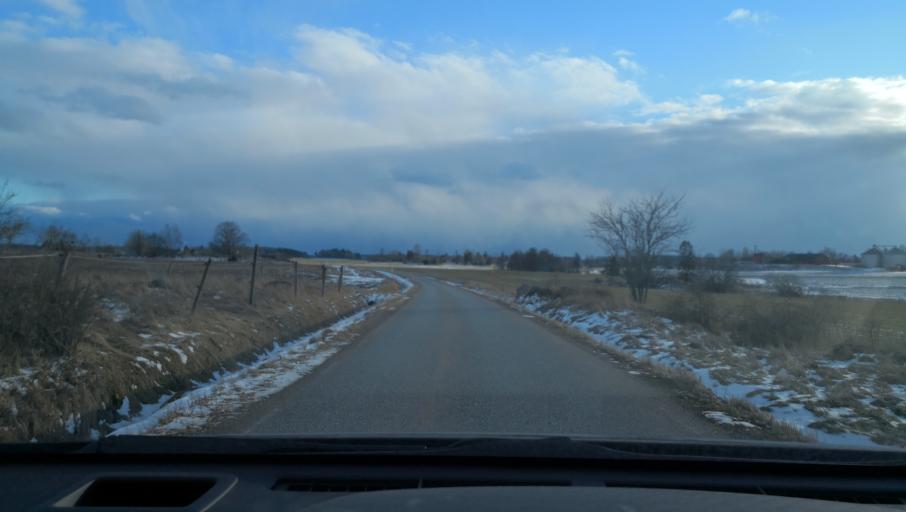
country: SE
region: Uppsala
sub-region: Enkopings Kommun
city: Irsta
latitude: 59.6948
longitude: 16.8589
